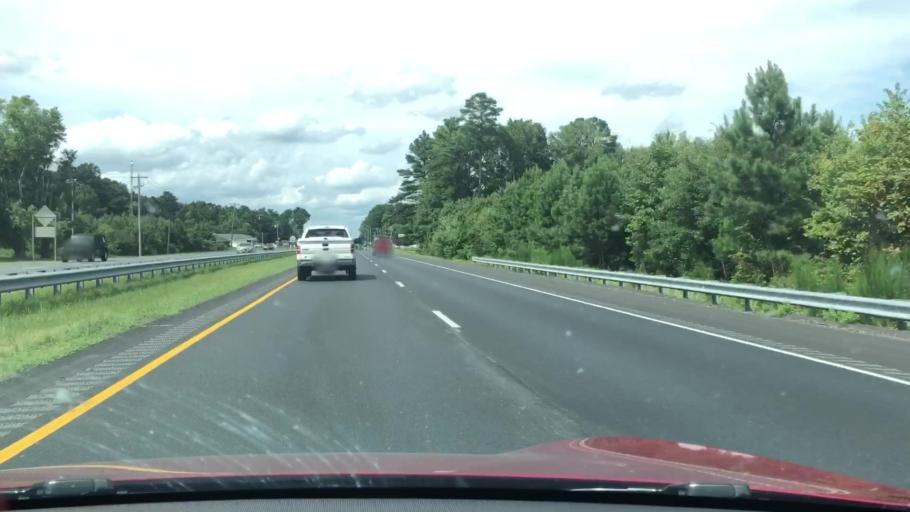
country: US
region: Maryland
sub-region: Worcester County
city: Pocomoke City
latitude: 38.0361
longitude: -75.5418
